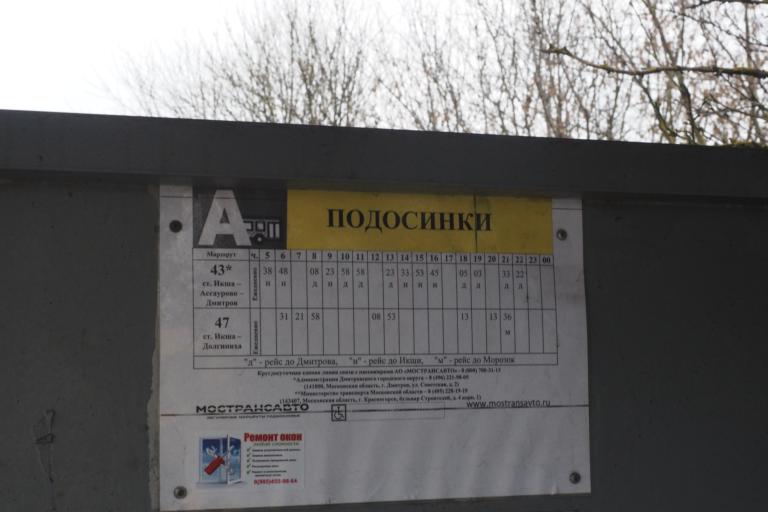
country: RU
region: Moskovskaya
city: Podosinki
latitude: 56.2054
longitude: 37.5435
